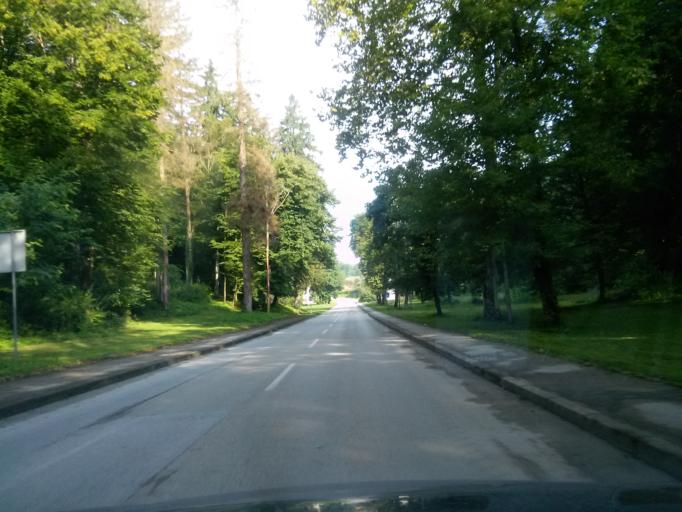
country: HR
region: Sisacko-Moslavacka
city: Gvozd
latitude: 45.2970
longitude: 15.9744
